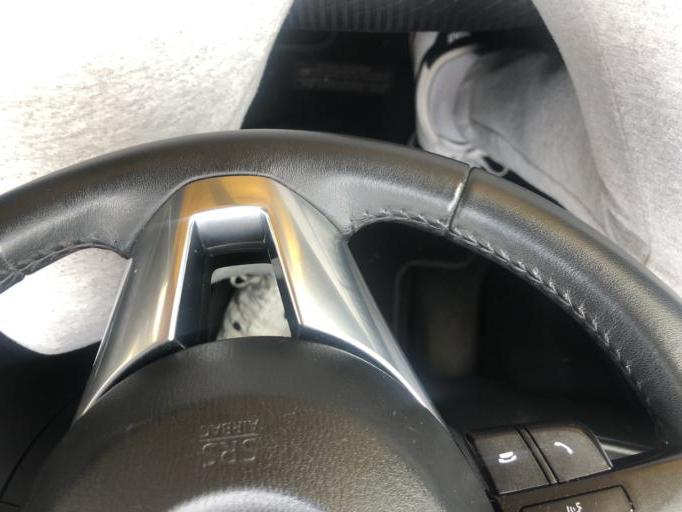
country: US
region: Tennessee
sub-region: Davidson County
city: Oak Hill
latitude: 36.1098
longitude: -86.7024
